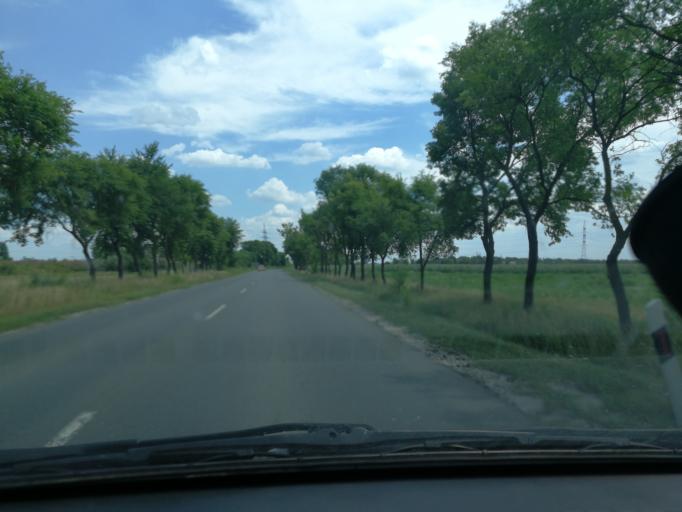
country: HU
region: Bacs-Kiskun
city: Solt
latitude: 46.8459
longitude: 19.0013
